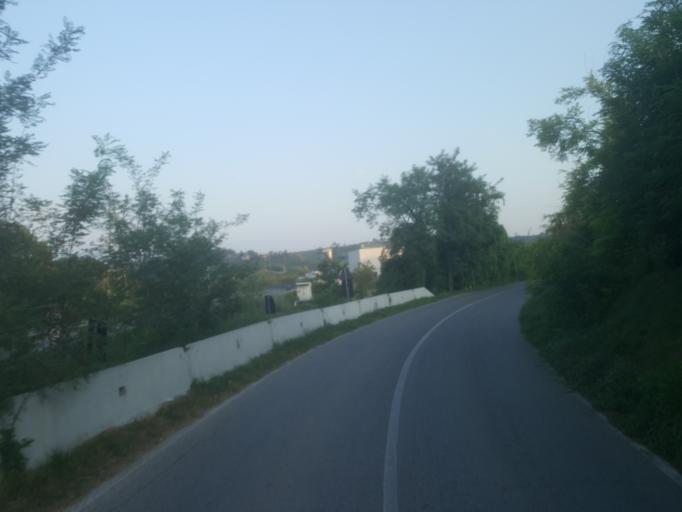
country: IT
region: Tuscany
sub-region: Province of Florence
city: Certaldo
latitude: 43.5386
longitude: 11.0345
